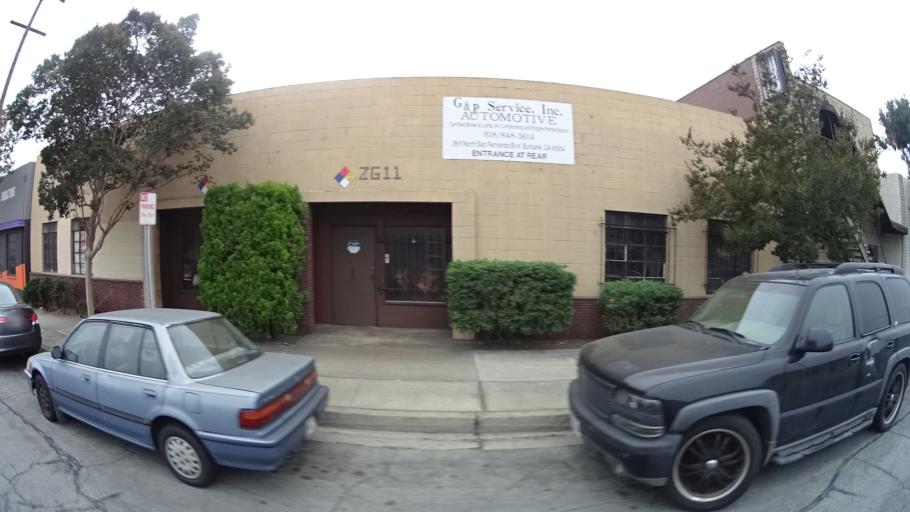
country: US
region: California
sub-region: Los Angeles County
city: Burbank
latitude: 34.1987
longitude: -118.3392
